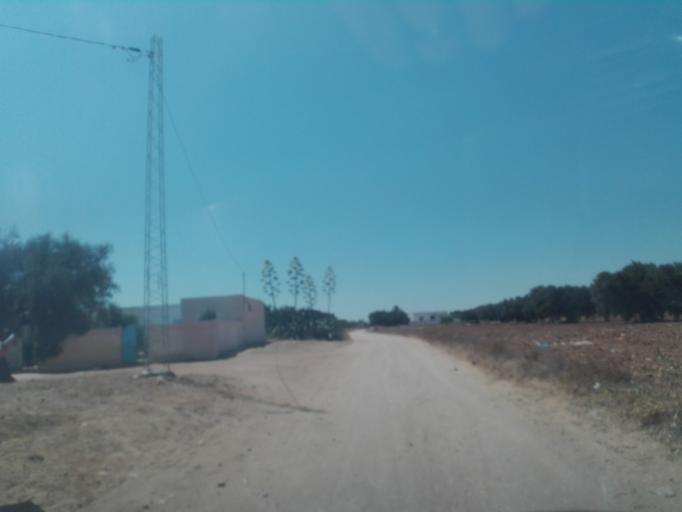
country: TN
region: Safaqis
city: Jabinyanah
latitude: 35.1072
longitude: 10.9079
